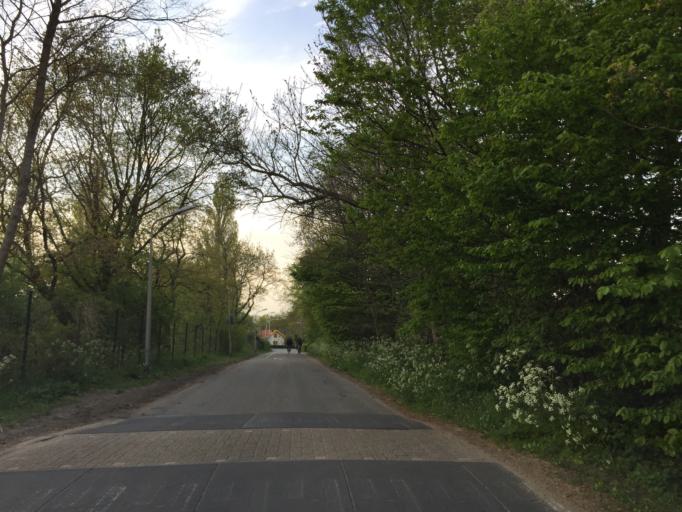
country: NL
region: South Holland
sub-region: Gemeente Leidschendam-Voorburg
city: Voorburg
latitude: 52.1068
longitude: 4.3387
